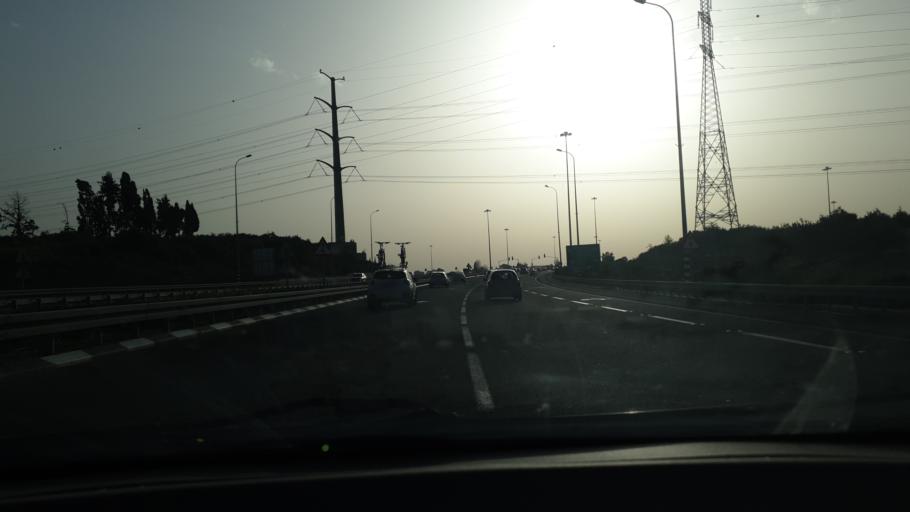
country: IL
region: Central District
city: Even Yehuda
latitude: 32.2564
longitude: 34.8967
